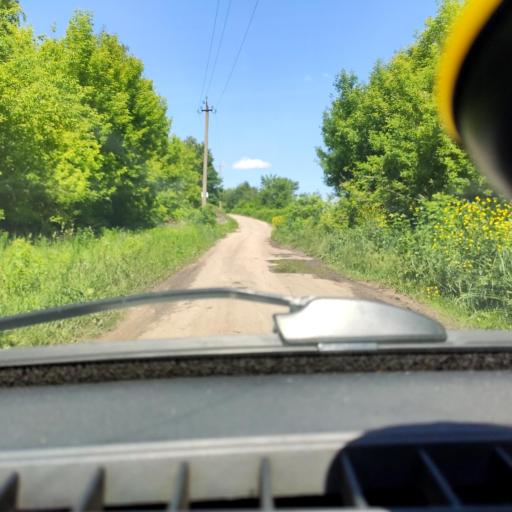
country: RU
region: Samara
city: Zhigulevsk
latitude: 53.3784
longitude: 49.5085
